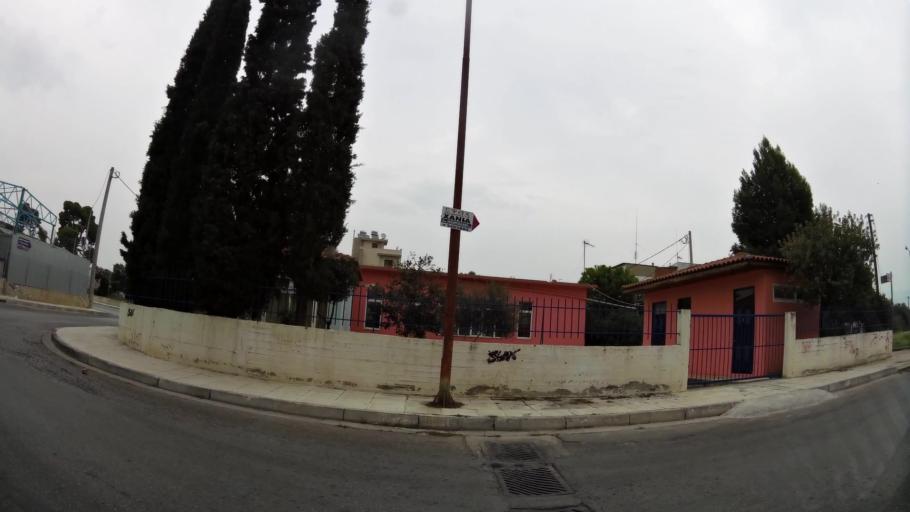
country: GR
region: Attica
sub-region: Nomos Piraios
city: Agios Ioannis Rentis
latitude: 37.9710
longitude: 23.6766
